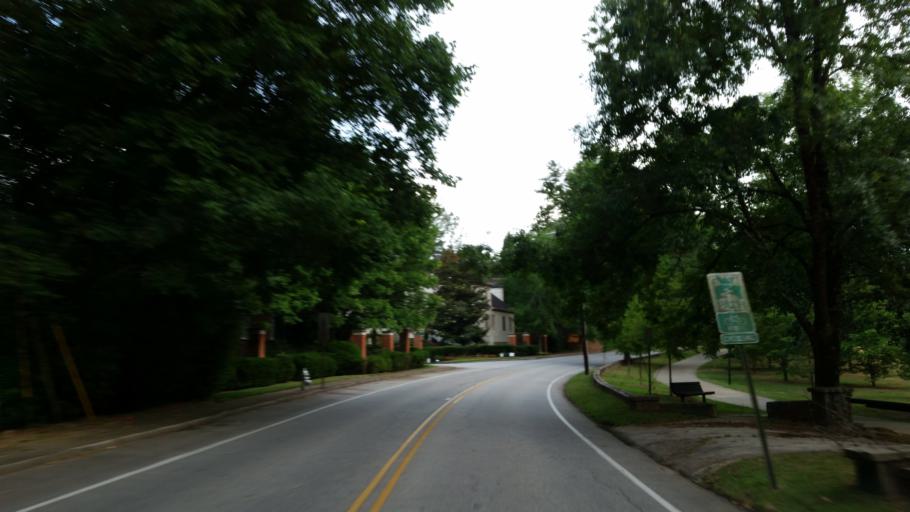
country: US
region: Georgia
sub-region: DeKalb County
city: North Atlanta
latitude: 33.8668
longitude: -84.3875
